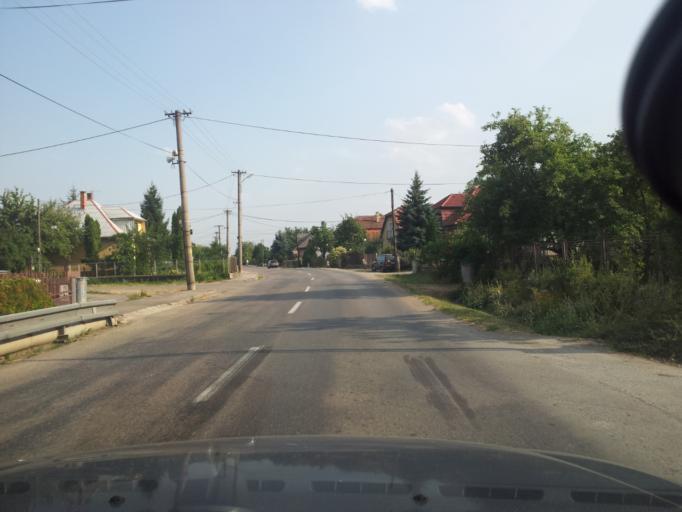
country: SK
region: Nitriansky
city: Banovce nad Bebravou
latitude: 48.8011
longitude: 18.1959
